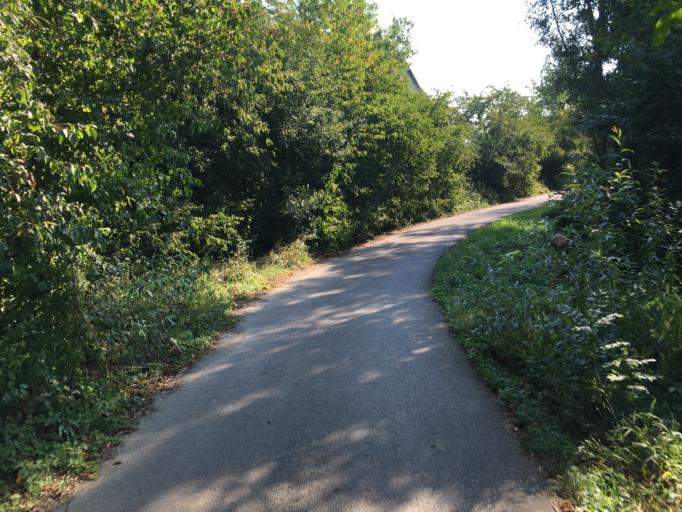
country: SK
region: Nitriansky
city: Puchov
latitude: 49.0650
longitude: 18.3566
